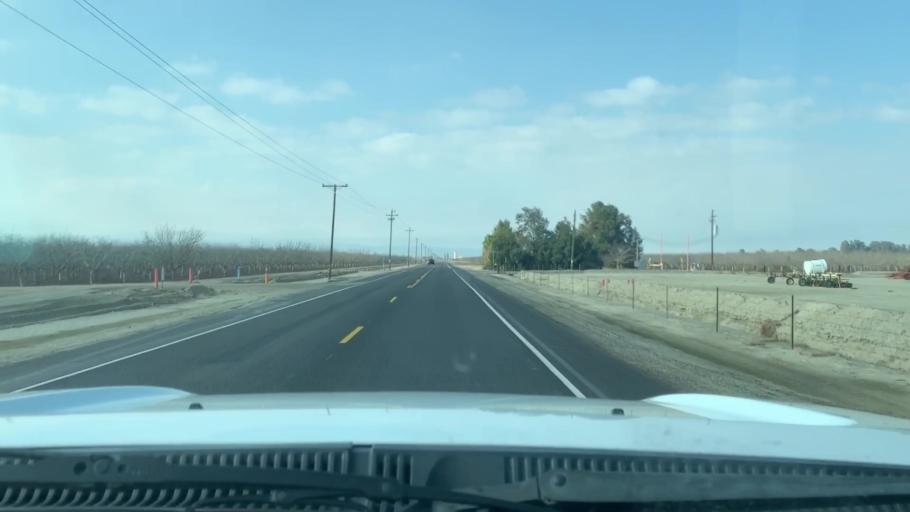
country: US
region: California
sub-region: Kern County
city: Buttonwillow
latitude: 35.4423
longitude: -119.4200
